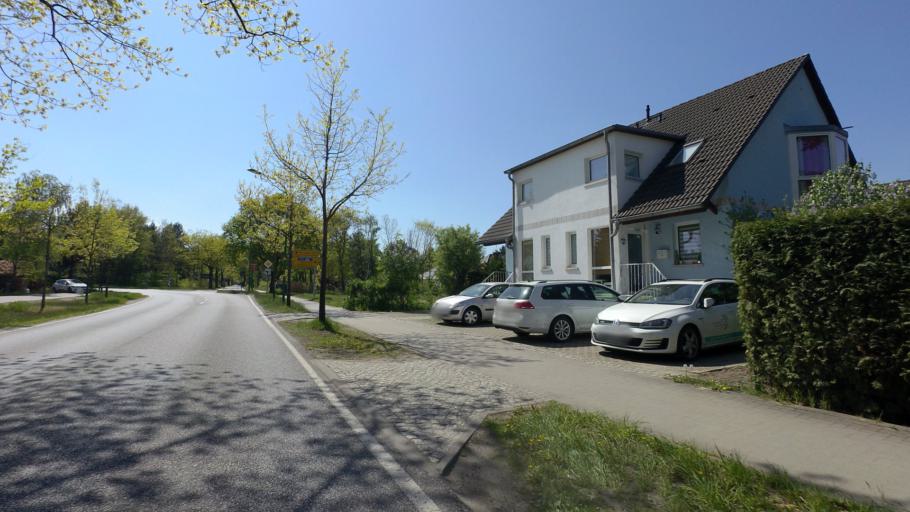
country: DE
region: Brandenburg
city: Bestensee
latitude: 52.2630
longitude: 13.6335
